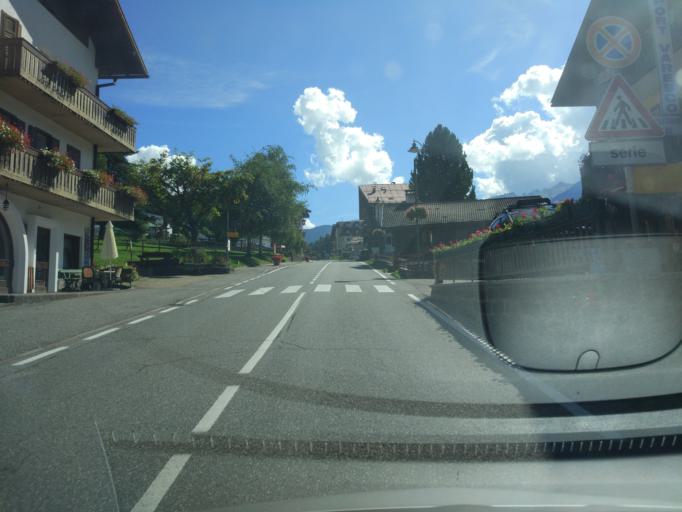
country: IT
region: Trentino-Alto Adige
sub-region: Provincia di Trento
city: Predazzo
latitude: 46.3135
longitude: 11.6611
